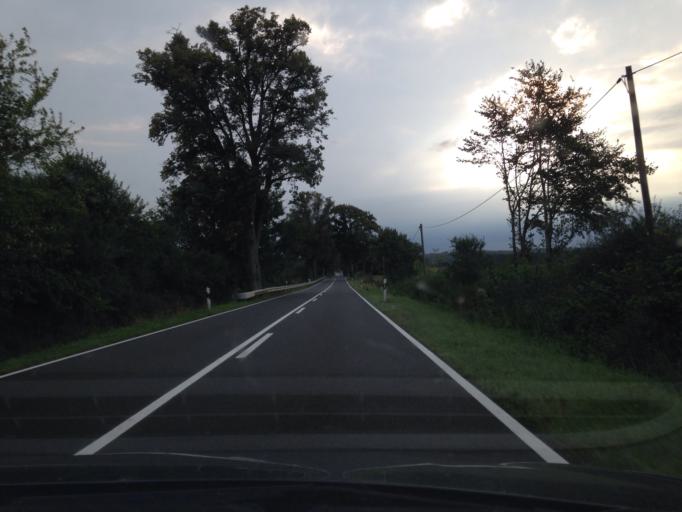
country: DE
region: Mecklenburg-Vorpommern
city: Carpin
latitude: 53.3652
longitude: 13.2719
